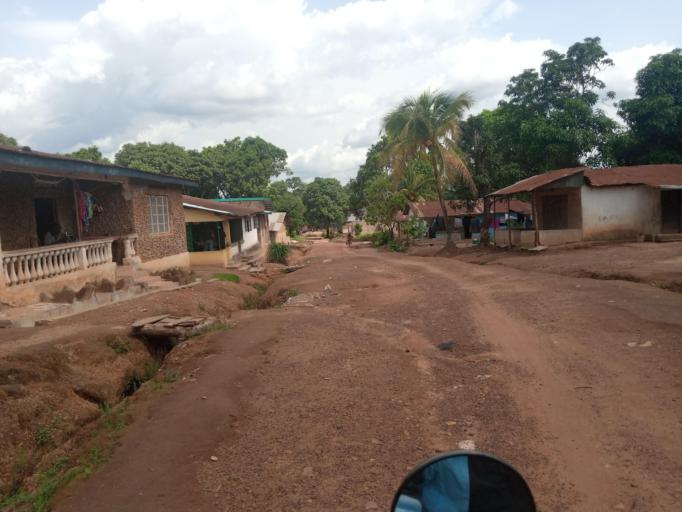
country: SL
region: Southern Province
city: Baoma
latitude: 7.9819
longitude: -11.7291
